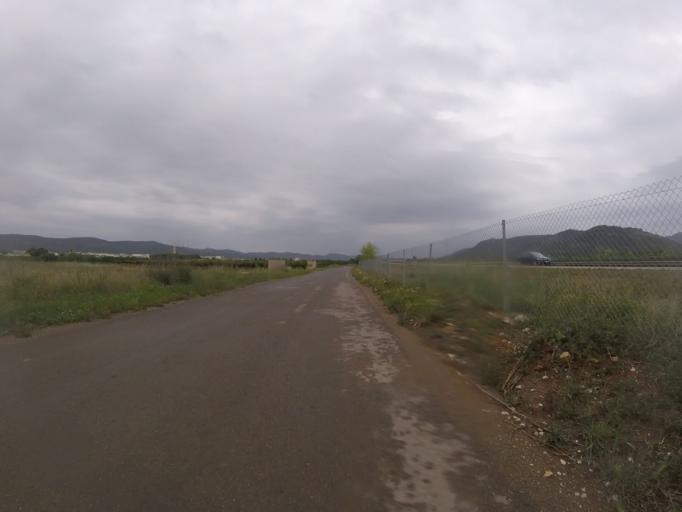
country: ES
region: Valencia
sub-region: Provincia de Castello
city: Alcala de Xivert
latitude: 40.2911
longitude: 0.2290
